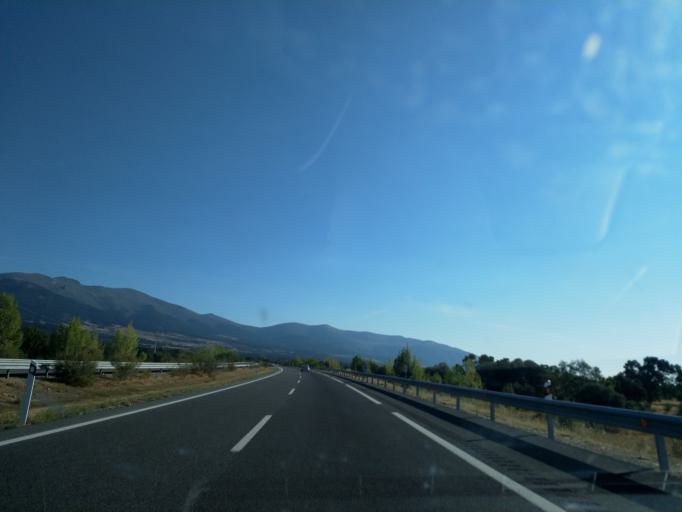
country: ES
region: Castille and Leon
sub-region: Provincia de Segovia
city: Segovia
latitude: 40.8872
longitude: -4.1166
